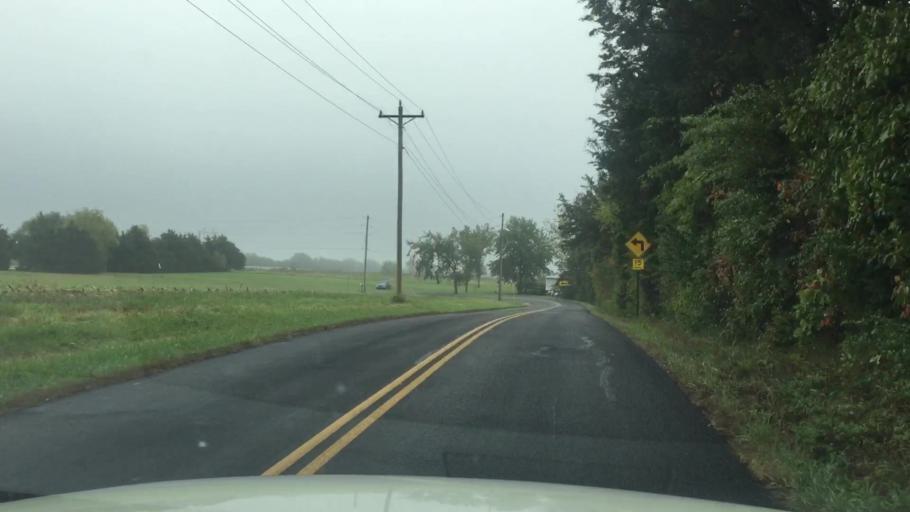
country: US
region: Missouri
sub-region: Boone County
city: Ashland
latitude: 38.8162
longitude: -92.2927
